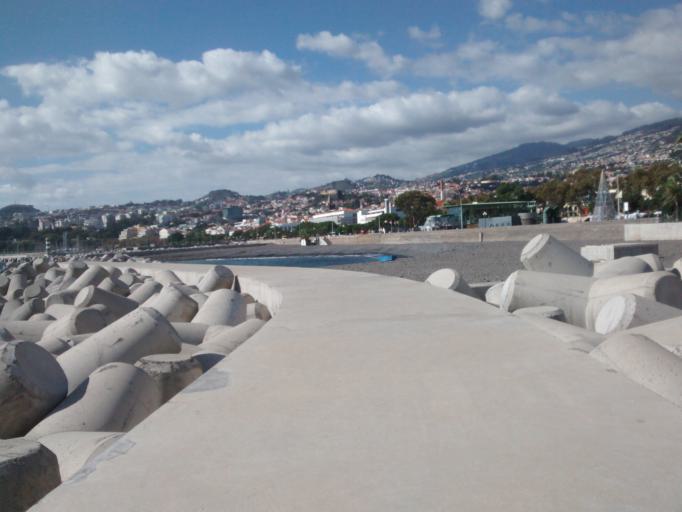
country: PT
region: Madeira
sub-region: Funchal
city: Funchal
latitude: 32.6460
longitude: -16.9000
